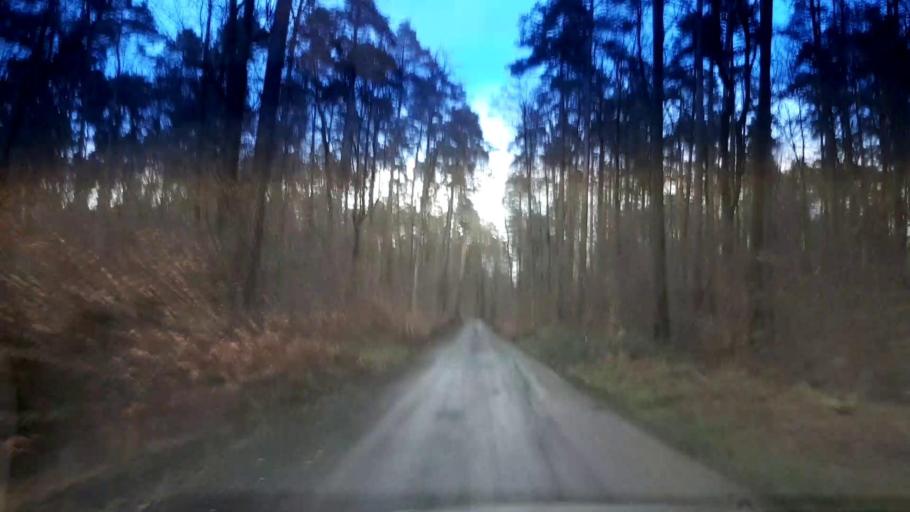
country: DE
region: Bavaria
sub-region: Regierungsbezirk Unterfranken
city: Stettfeld
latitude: 49.9758
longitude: 10.7447
